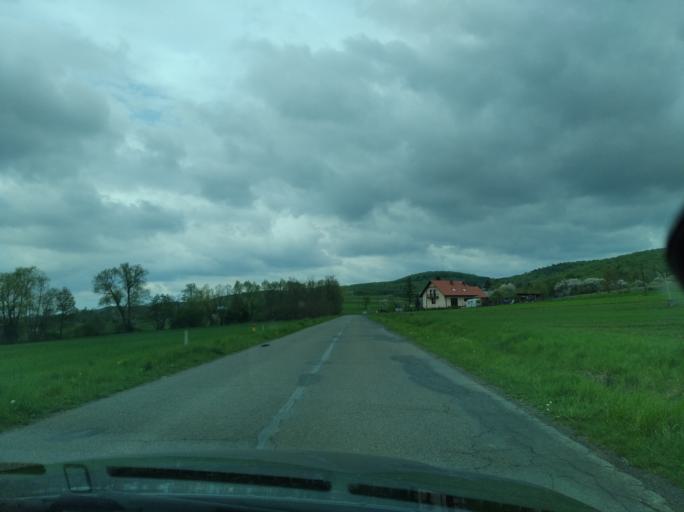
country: PL
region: Subcarpathian Voivodeship
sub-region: Powiat sanocki
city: Dlugie
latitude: 49.6085
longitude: 22.0468
